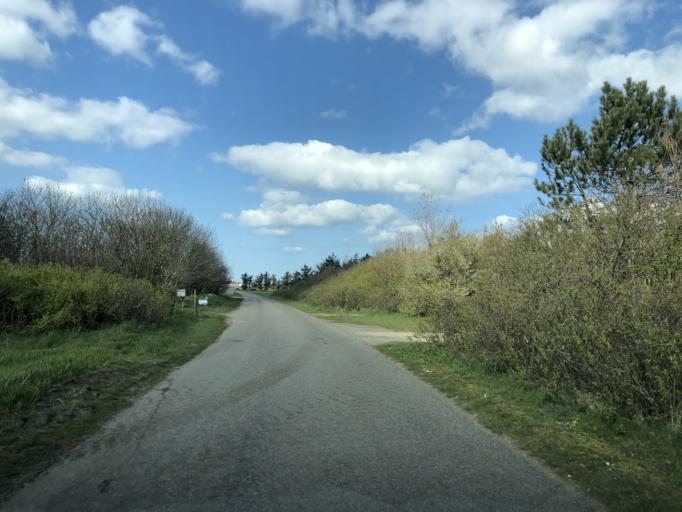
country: DK
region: Central Jutland
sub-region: Holstebro Kommune
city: Ulfborg
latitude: 56.3927
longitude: 8.1913
